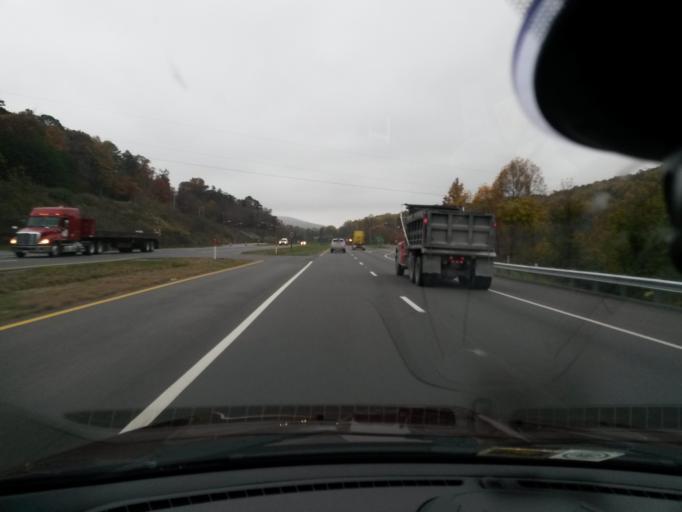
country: US
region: Virginia
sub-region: Botetourt County
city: Cloverdale
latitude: 37.3501
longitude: -79.8833
